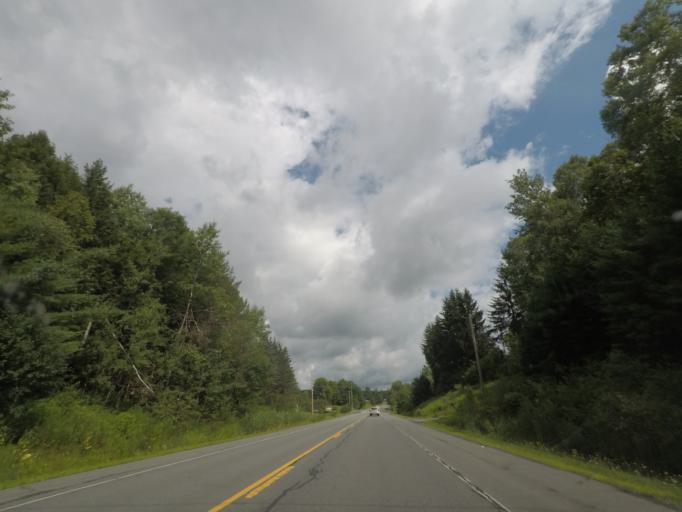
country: US
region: Massachusetts
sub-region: Berkshire County
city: Lanesborough
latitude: 42.5549
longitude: -73.3745
